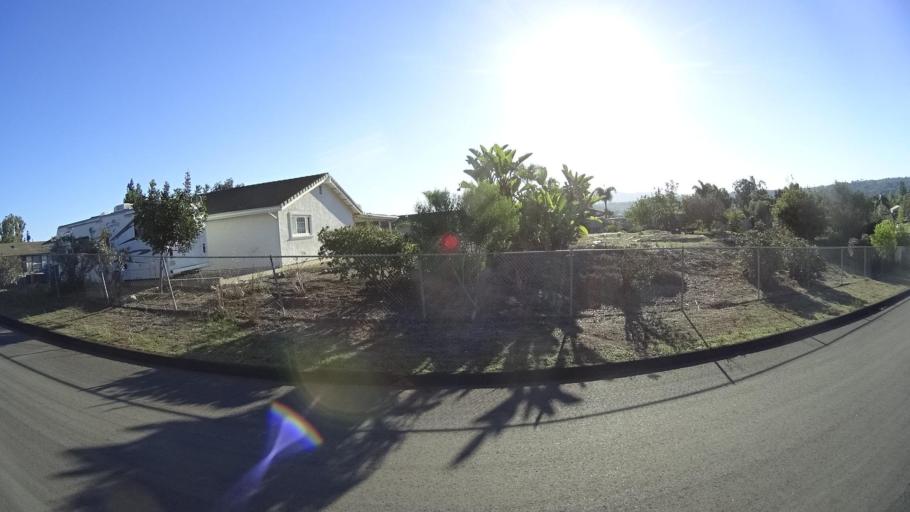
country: US
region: California
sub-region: San Diego County
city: Bonita
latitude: 32.6716
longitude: -117.0333
